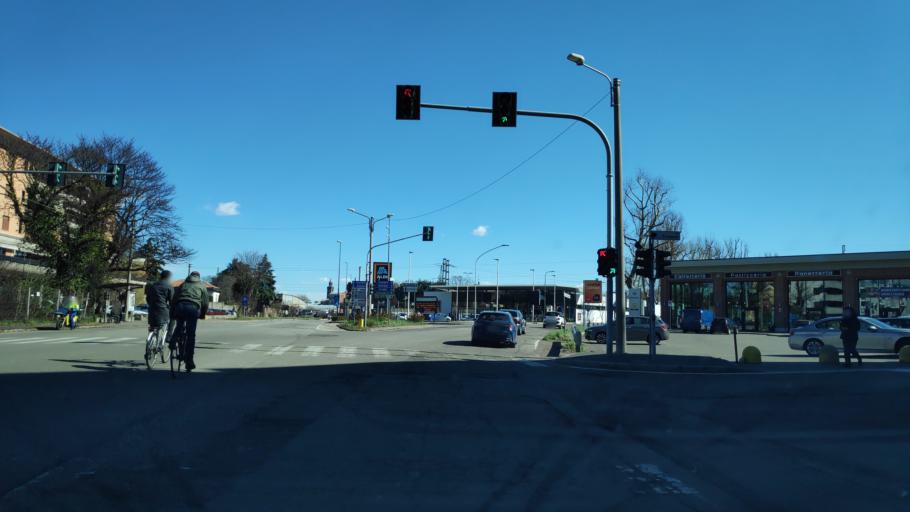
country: IT
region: Lombardy
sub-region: Provincia di Varese
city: Castellanza
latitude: 45.6150
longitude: 8.8844
